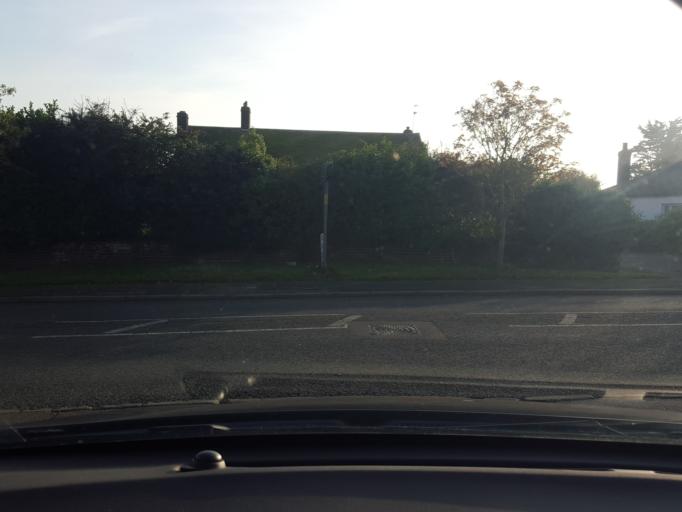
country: GB
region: England
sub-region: Essex
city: Walton-on-the-Naze
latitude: 51.8499
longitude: 1.2560
